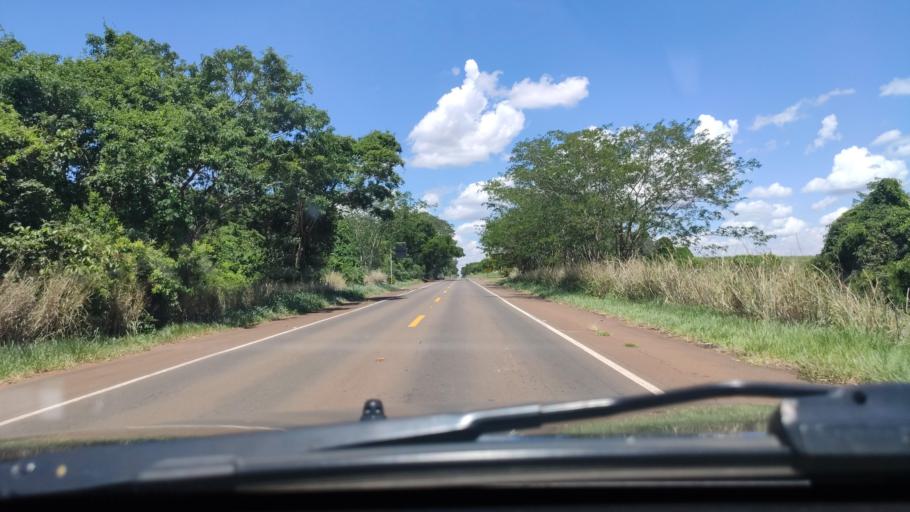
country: BR
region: Sao Paulo
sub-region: Boa Esperanca Do Sul
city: Boa Esperanca do Sul
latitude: -22.0693
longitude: -48.3873
